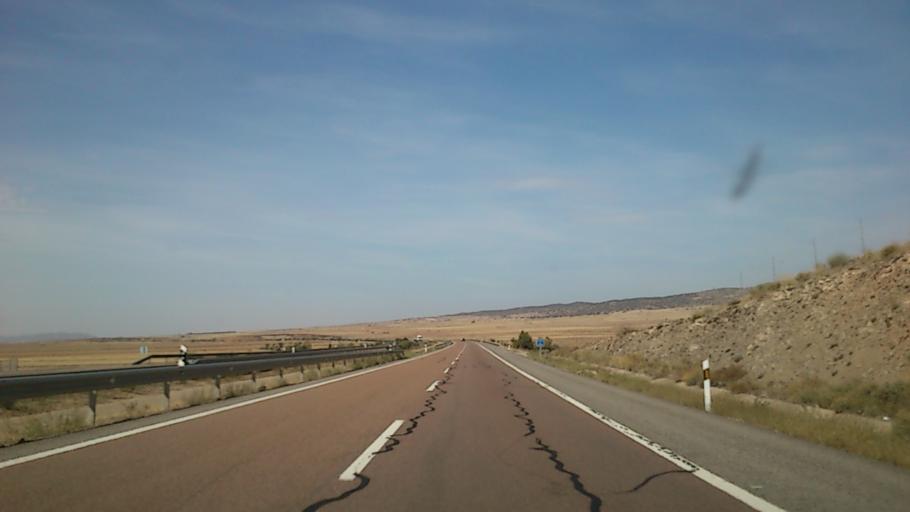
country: ES
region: Aragon
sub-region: Provincia de Teruel
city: Singra
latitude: 40.6634
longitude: -1.3164
